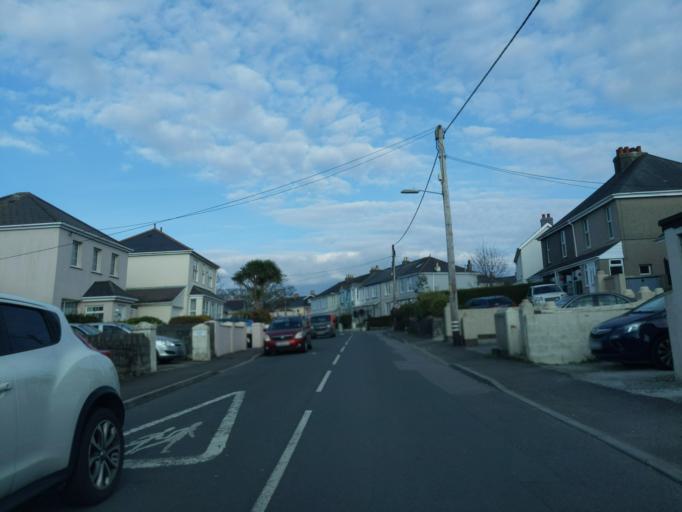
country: GB
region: England
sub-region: Cornwall
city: Saltash
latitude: 50.4059
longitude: -4.2260
